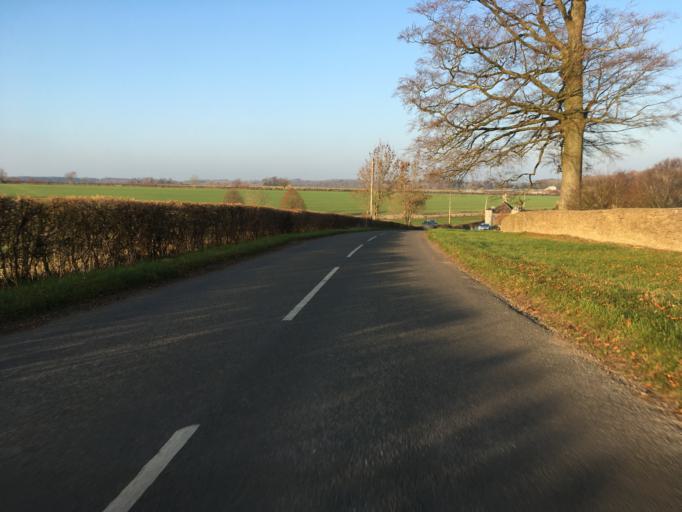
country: GB
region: England
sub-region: Wiltshire
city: Luckington
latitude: 51.5521
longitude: -2.2930
